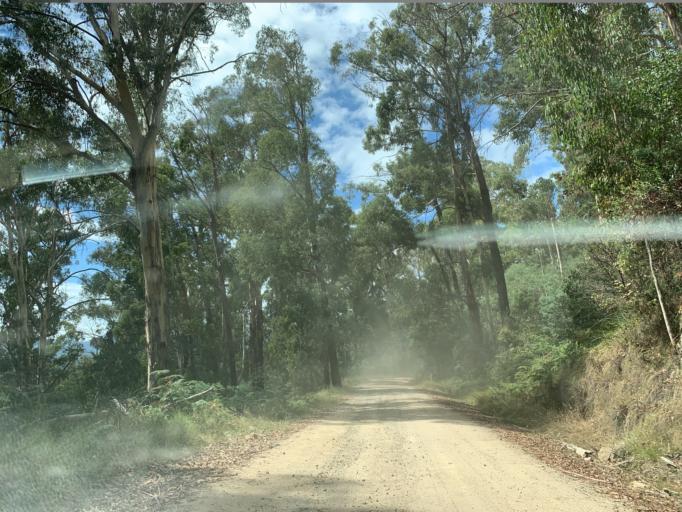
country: AU
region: Victoria
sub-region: Mansfield
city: Mansfield
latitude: -37.0990
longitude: 146.5072
